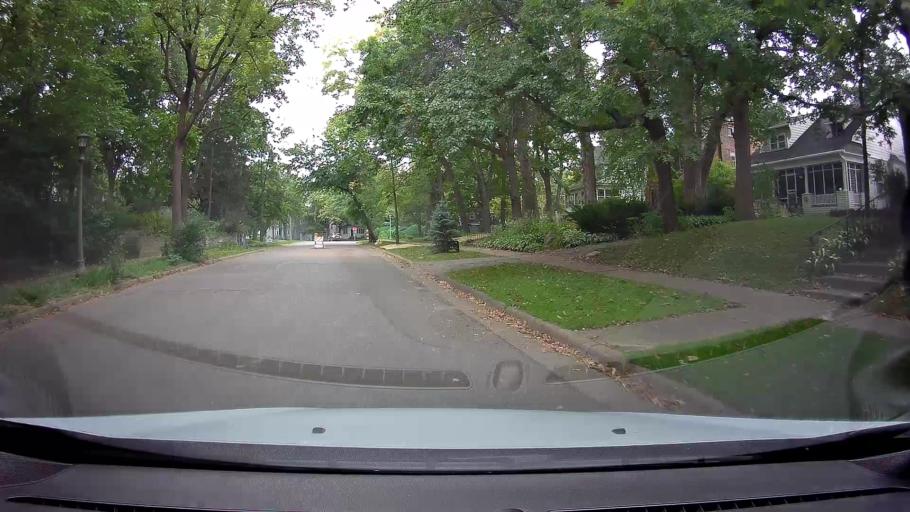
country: US
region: Minnesota
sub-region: Ramsey County
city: Lauderdale
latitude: 44.9811
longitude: -93.1983
